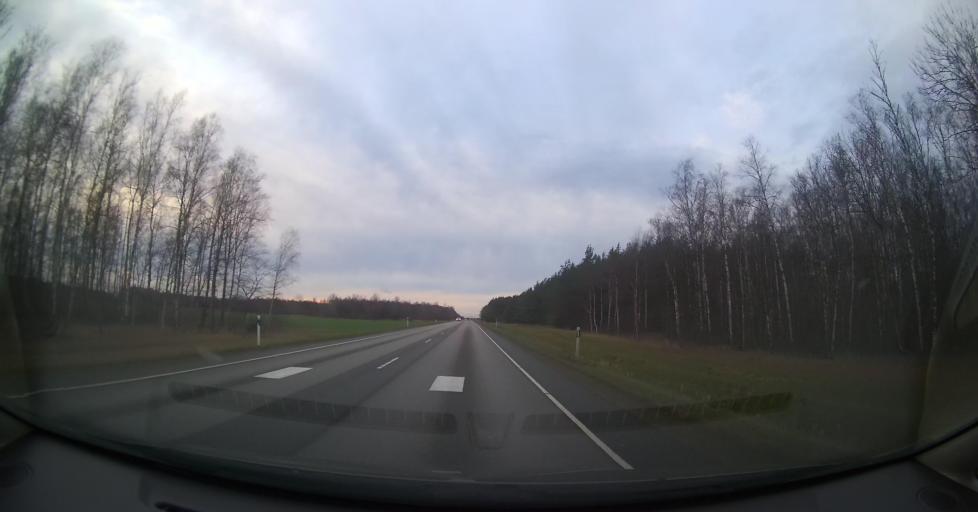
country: EE
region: Ida-Virumaa
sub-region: Kohtla-Jaerve linn
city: Kohtla-Jarve
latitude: 59.4195
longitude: 27.2538
